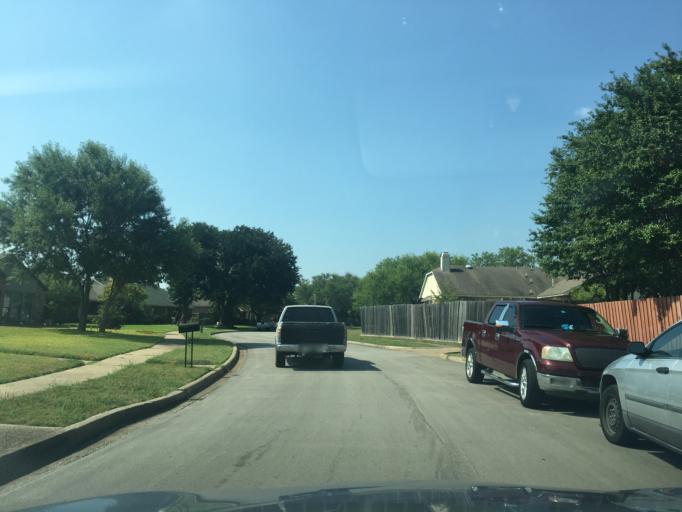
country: US
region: Texas
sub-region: Dallas County
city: Garland
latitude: 32.9454
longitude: -96.6264
